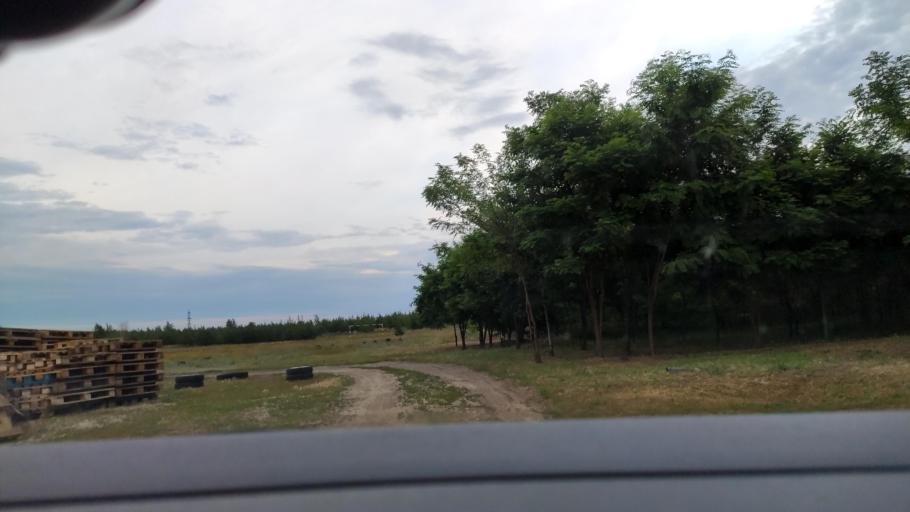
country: RU
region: Voronezj
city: Maslovka
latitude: 51.5673
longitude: 39.2513
